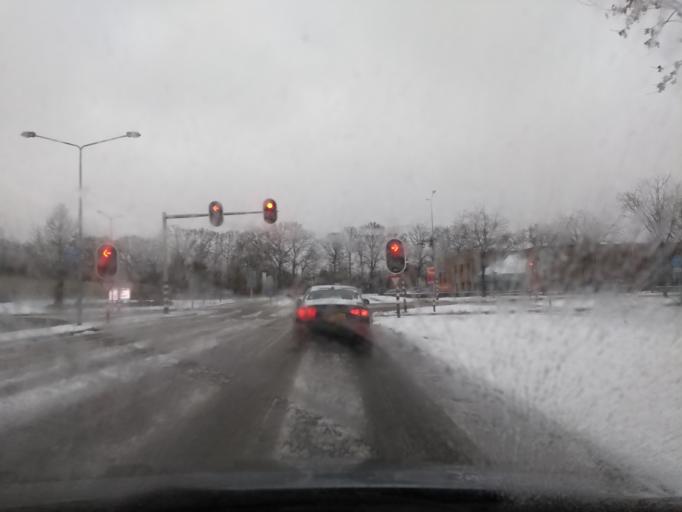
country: NL
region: Overijssel
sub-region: Gemeente Almelo
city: Almelo
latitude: 52.3745
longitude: 6.6513
